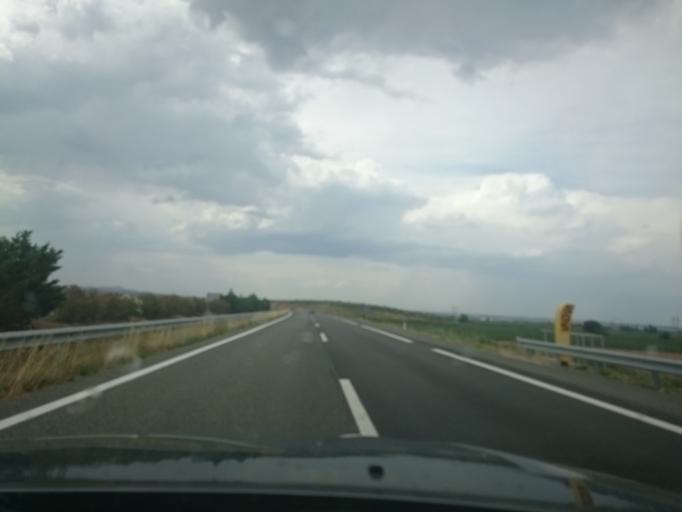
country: ES
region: Navarre
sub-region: Provincia de Navarra
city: Corella
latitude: 42.1432
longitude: -1.7834
